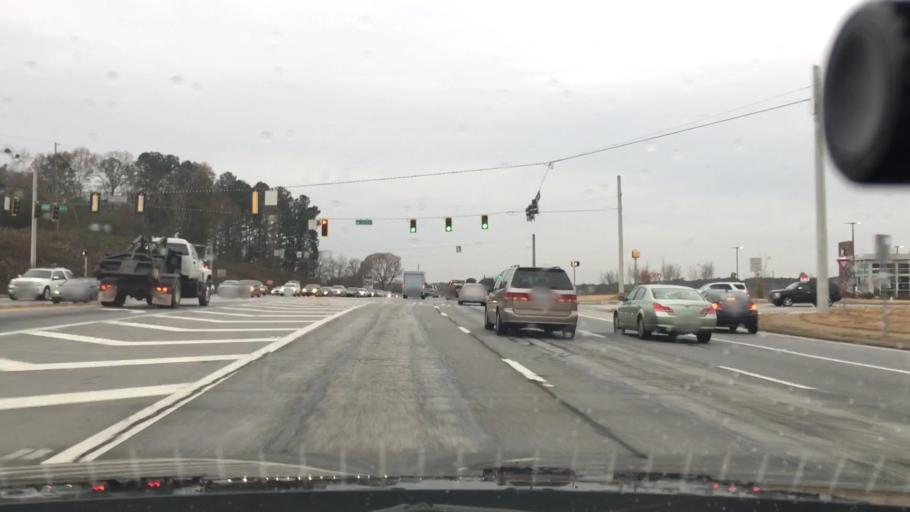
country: US
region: Georgia
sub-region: Fayette County
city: Peachtree City
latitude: 33.3968
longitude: -84.6181
